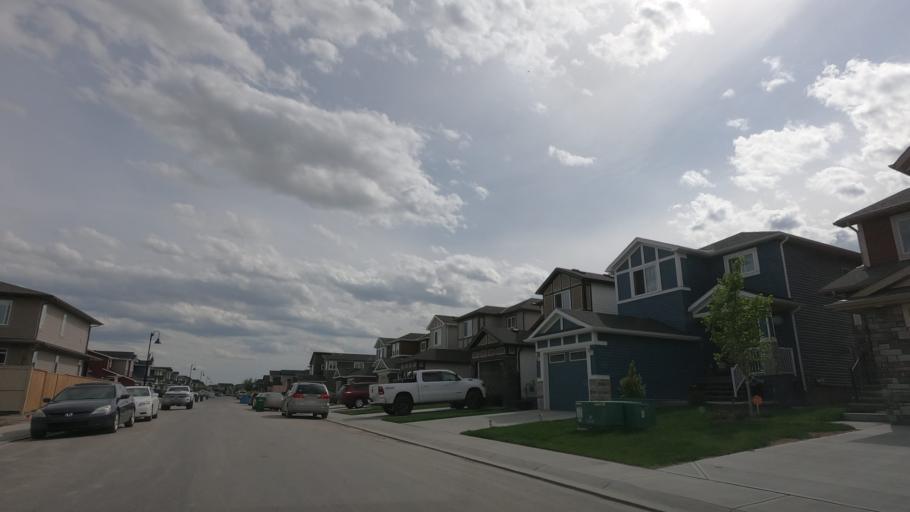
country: CA
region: Alberta
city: Airdrie
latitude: 51.2782
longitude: -114.0426
